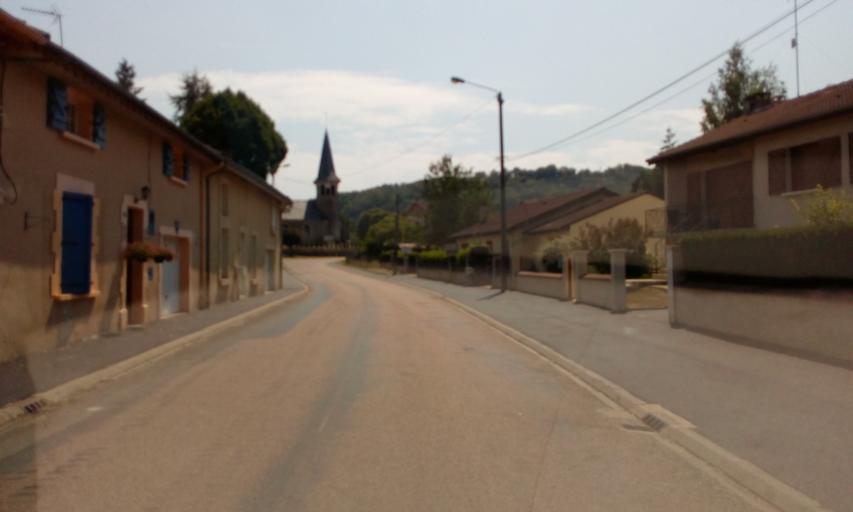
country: FR
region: Lorraine
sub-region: Departement de la Meuse
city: Dieue-sur-Meuse
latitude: 49.1462
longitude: 5.5239
